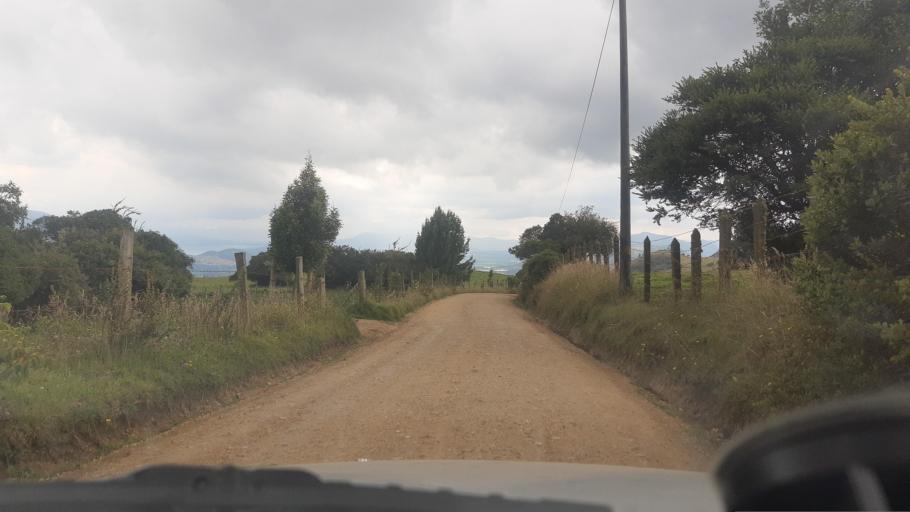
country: CO
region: Cundinamarca
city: Suesca
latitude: 5.1330
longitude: -73.7829
